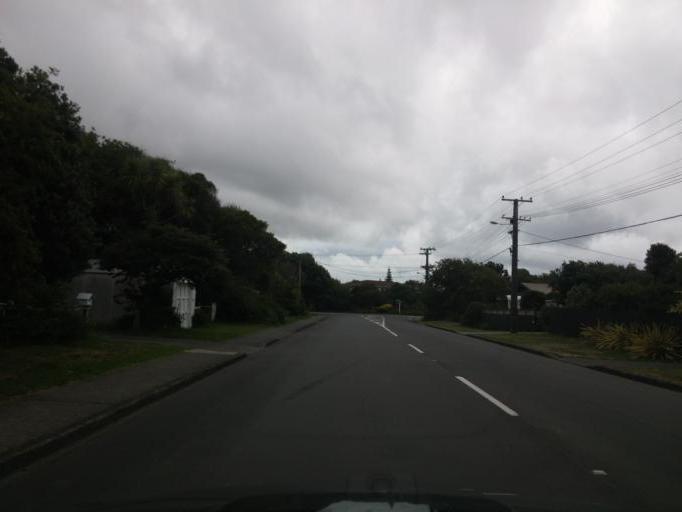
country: NZ
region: Wellington
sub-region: Kapiti Coast District
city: Paraparaumu
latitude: -40.8671
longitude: 175.0243
